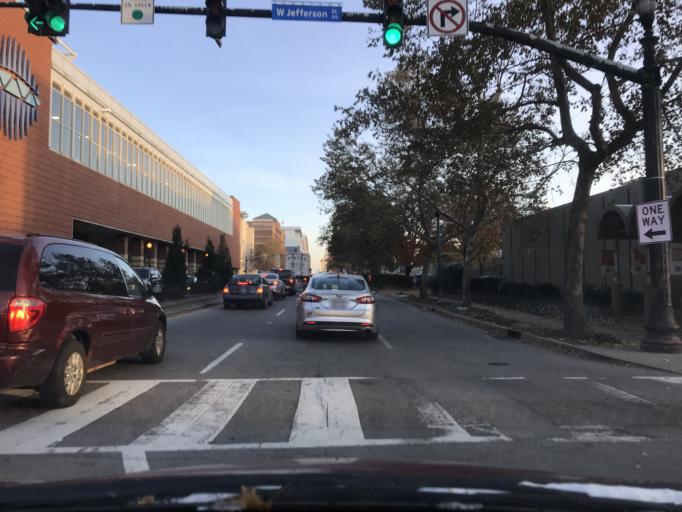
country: US
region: Kentucky
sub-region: Jefferson County
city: Louisville
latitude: 38.2535
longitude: -85.7537
